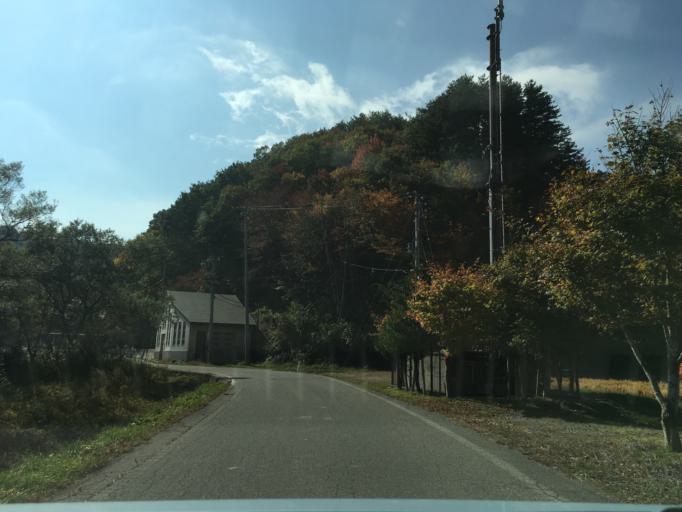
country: JP
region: Fukushima
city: Inawashiro
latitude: 37.4801
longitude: 140.0297
